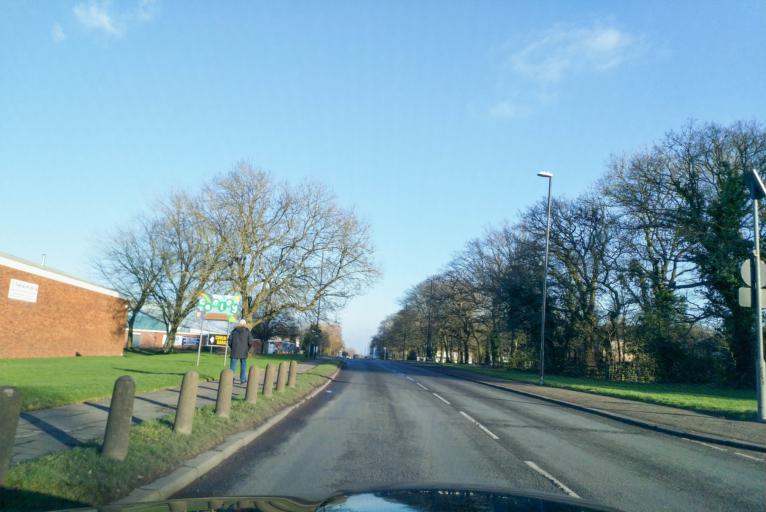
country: GB
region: England
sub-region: Warwickshire
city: Kenilworth
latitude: 52.3928
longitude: -1.5924
